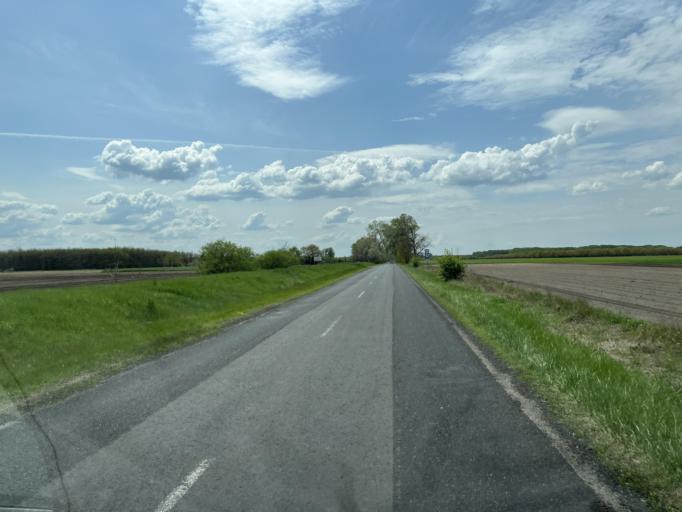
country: HU
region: Pest
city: Cegled
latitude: 47.1491
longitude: 19.7565
